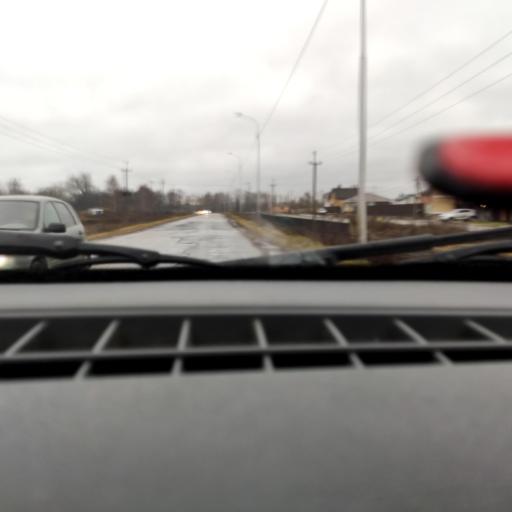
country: RU
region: Bashkortostan
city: Ufa
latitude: 54.6624
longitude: 55.9187
